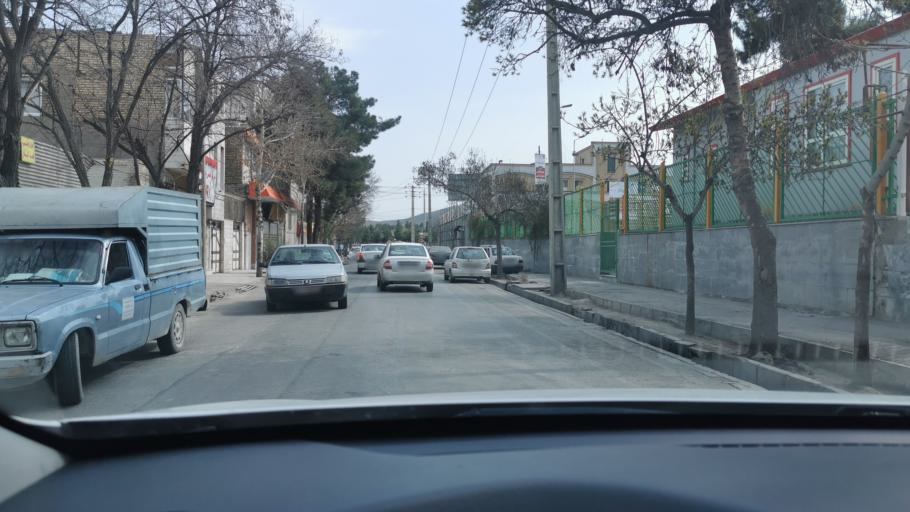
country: IR
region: Razavi Khorasan
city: Mashhad
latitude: 36.2739
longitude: 59.5690
